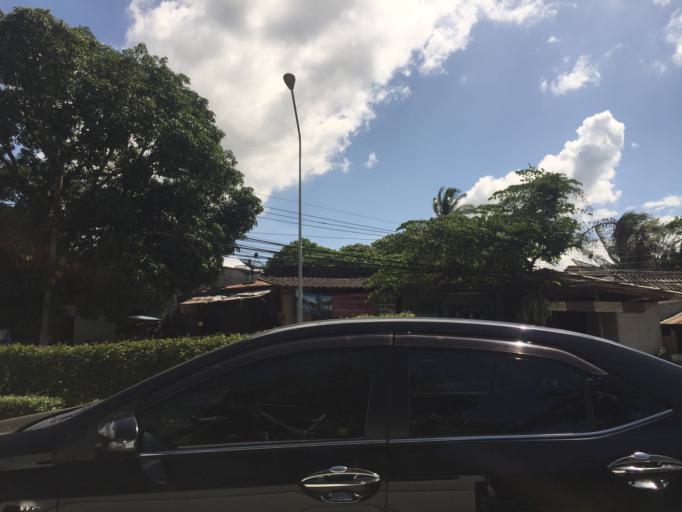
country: TH
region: Phangnga
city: Ban Ao Nang
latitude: 8.0412
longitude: 98.8364
